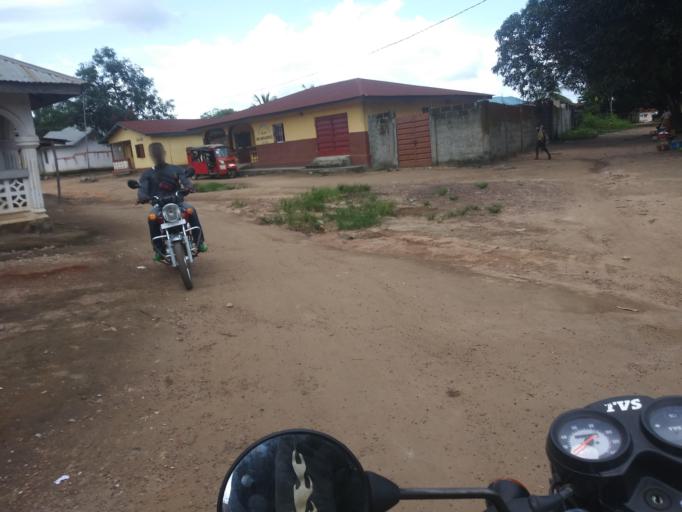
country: SL
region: Northern Province
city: Makeni
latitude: 8.8732
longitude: -12.0405
